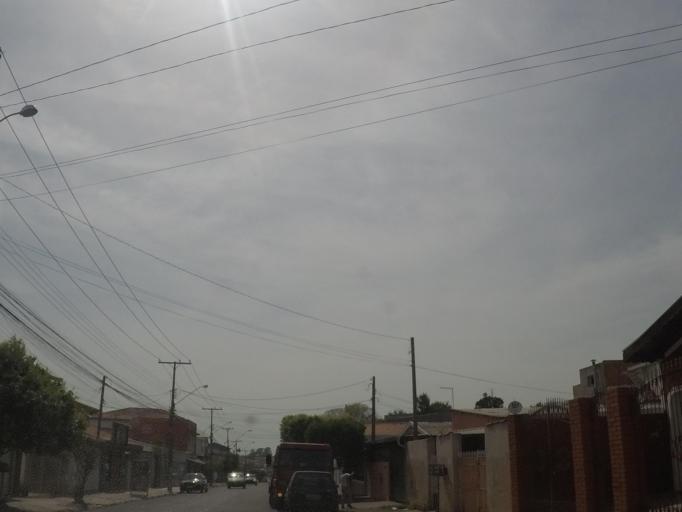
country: BR
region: Sao Paulo
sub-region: Hortolandia
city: Hortolandia
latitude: -22.8519
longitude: -47.1898
